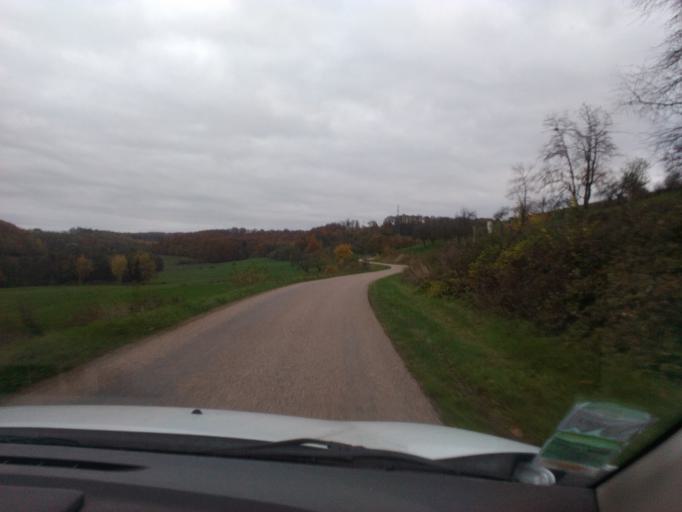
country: FR
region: Lorraine
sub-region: Departement des Vosges
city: Mirecourt
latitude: 48.3093
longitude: 6.2112
